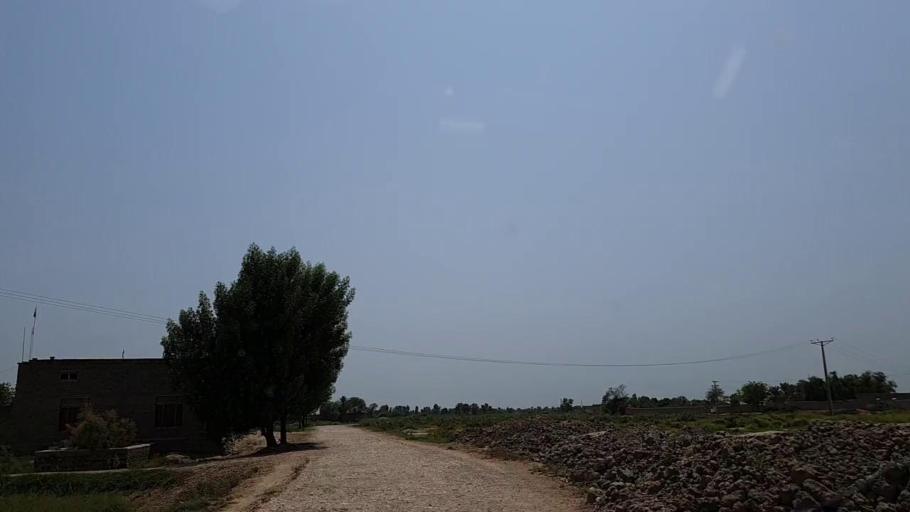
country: PK
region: Sindh
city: Adilpur
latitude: 27.9730
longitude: 69.3981
